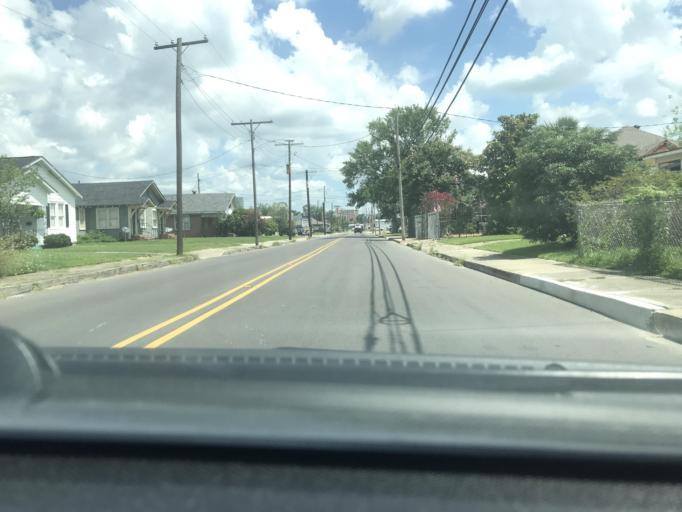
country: US
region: Louisiana
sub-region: Calcasieu Parish
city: Lake Charles
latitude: 30.2174
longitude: -93.2160
